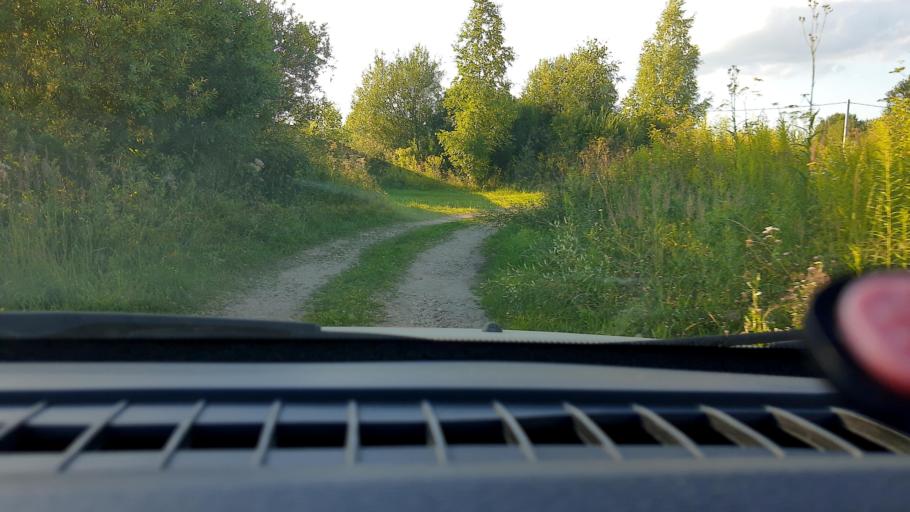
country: RU
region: Nizjnij Novgorod
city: Burevestnik
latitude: 56.0438
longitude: 43.8825
